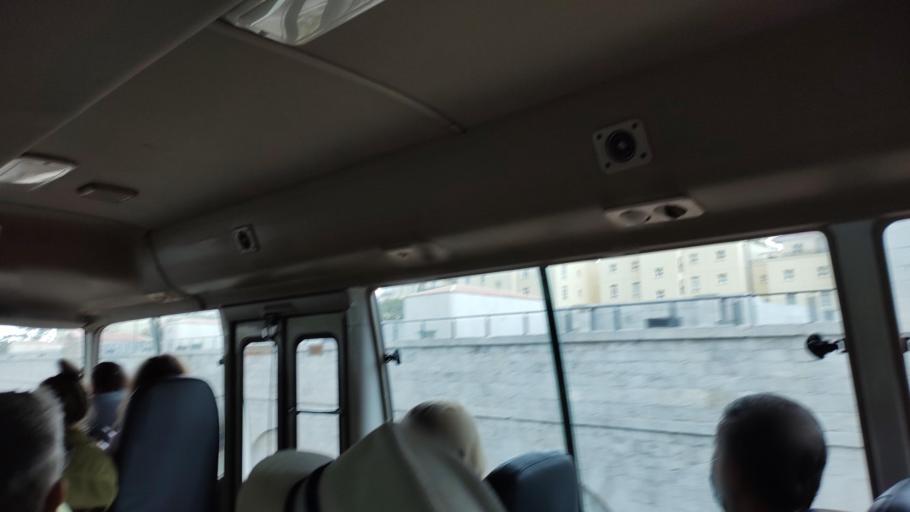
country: GI
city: Gibraltar
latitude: 36.1375
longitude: -5.3545
